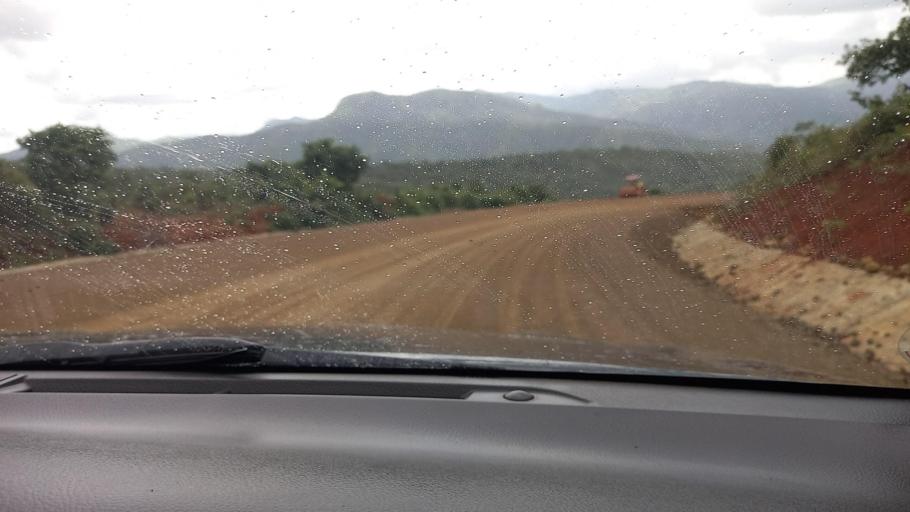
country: ET
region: Southern Nations, Nationalities, and People's Region
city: Mizan Teferi
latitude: 6.1809
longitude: 35.6969
